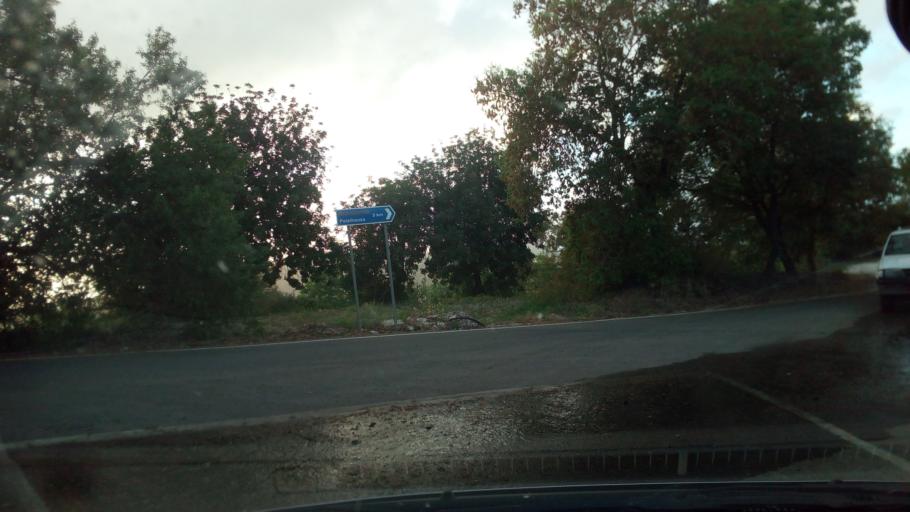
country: CY
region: Pafos
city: Polis
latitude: 34.9990
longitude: 32.5091
